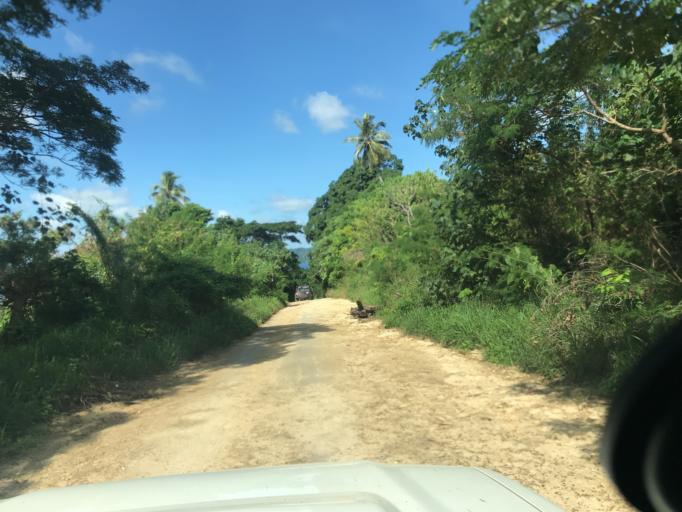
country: VU
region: Sanma
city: Luganville
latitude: -15.5246
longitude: 167.1488
